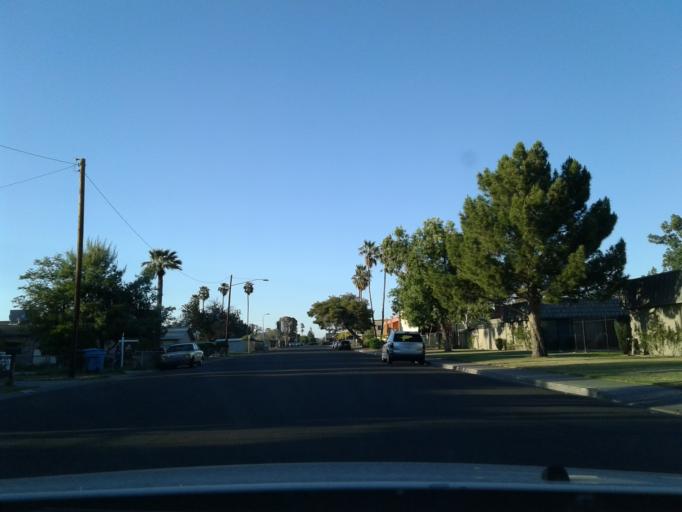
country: US
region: Arizona
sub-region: Maricopa County
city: Phoenix
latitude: 33.5070
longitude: -112.1042
